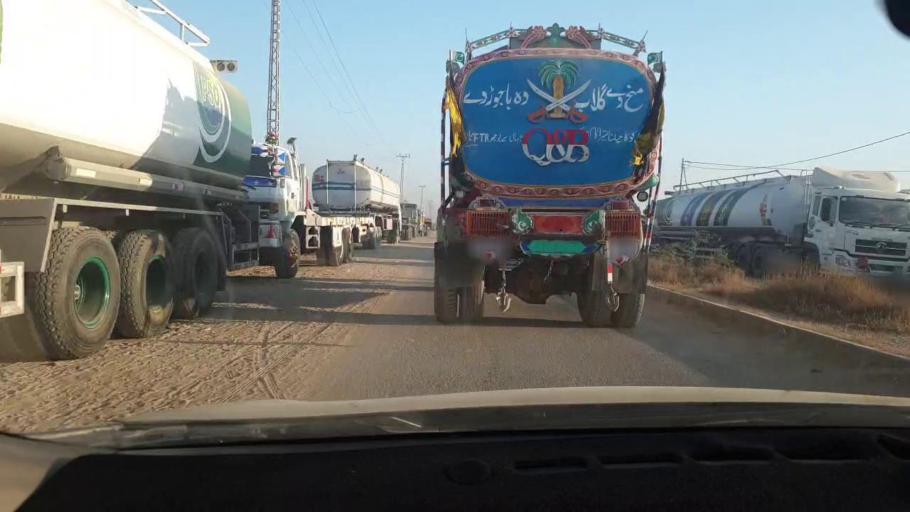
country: PK
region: Sindh
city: Malir Cantonment
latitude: 25.0162
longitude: 67.1710
